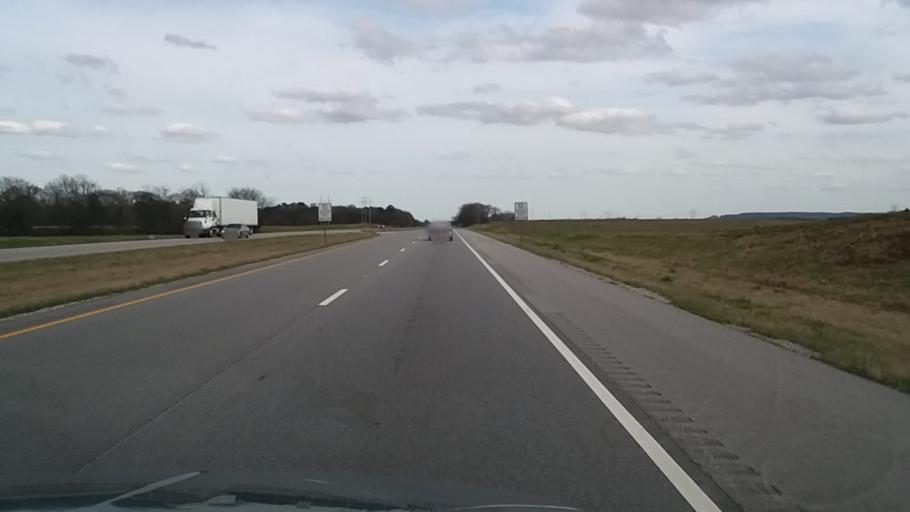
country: US
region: Alabama
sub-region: Lawrence County
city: Town Creek
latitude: 34.6826
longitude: -87.4747
